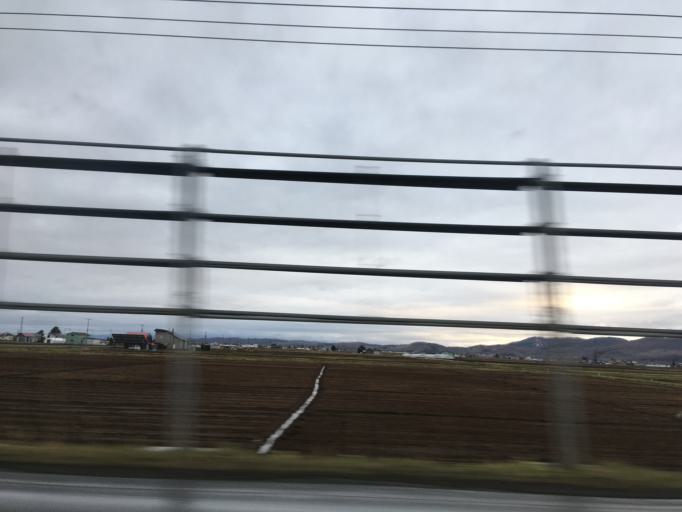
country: JP
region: Hokkaido
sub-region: Asahikawa-shi
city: Asahikawa
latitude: 43.9056
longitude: 142.5027
